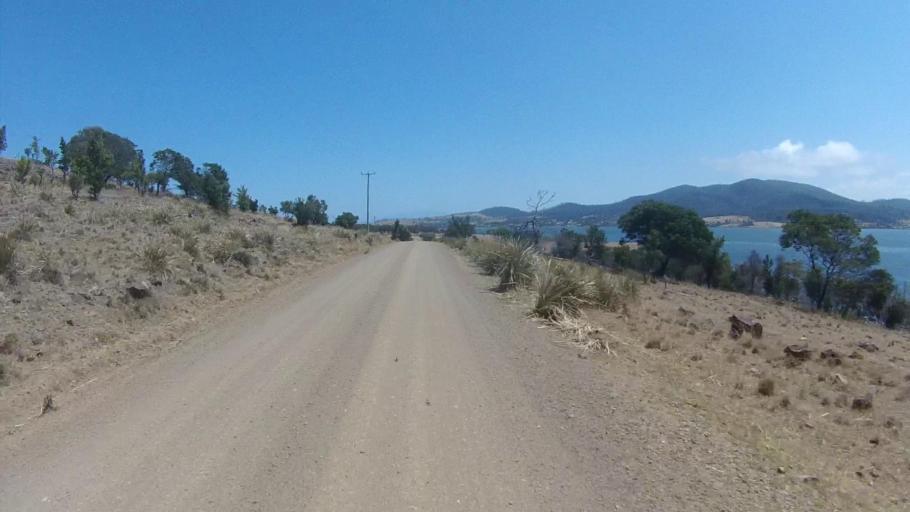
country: AU
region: Tasmania
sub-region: Sorell
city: Sorell
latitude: -42.8918
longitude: 147.8497
